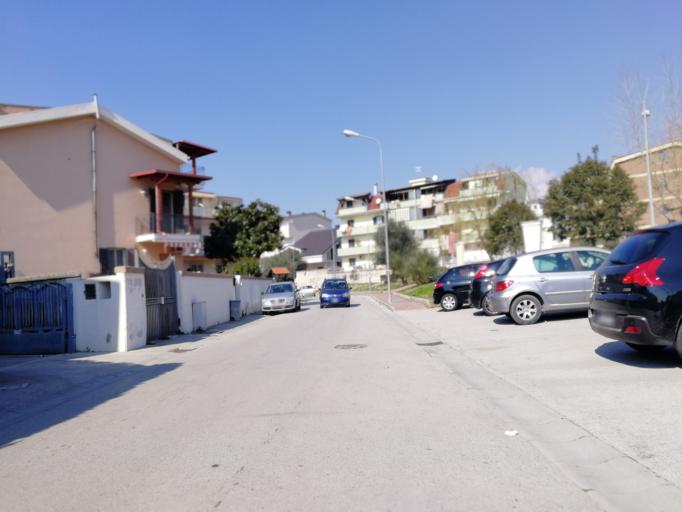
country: IT
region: Campania
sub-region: Provincia di Caserta
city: San Prisco
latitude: 41.0888
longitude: 14.2733
